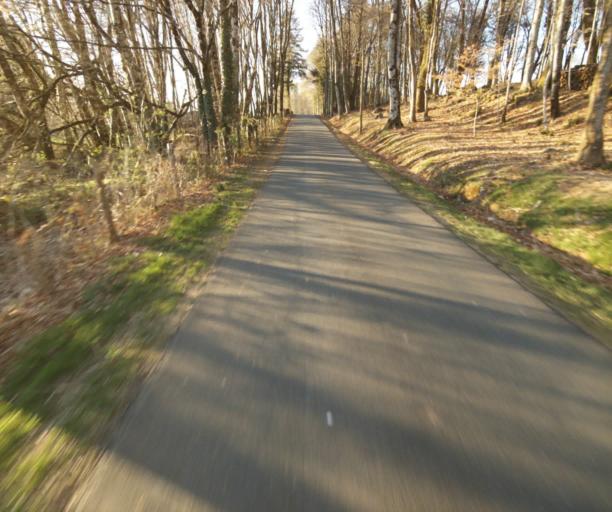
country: FR
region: Limousin
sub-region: Departement de la Correze
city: Seilhac
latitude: 45.3526
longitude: 1.7092
